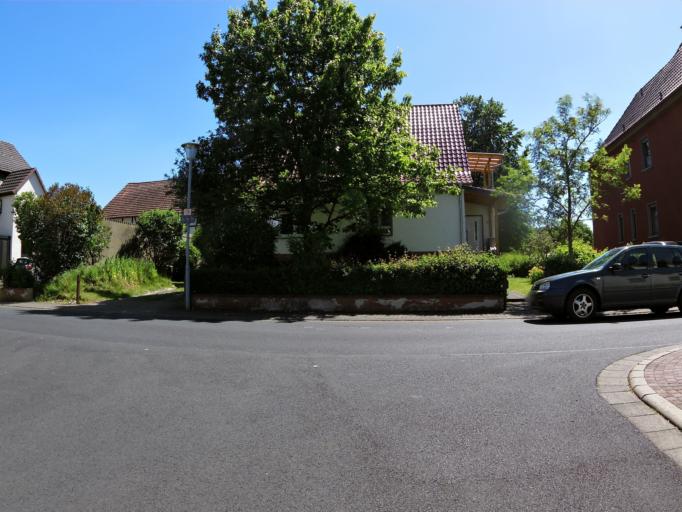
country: DE
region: Thuringia
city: Dankmarshausen
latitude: 50.9478
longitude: 10.0337
